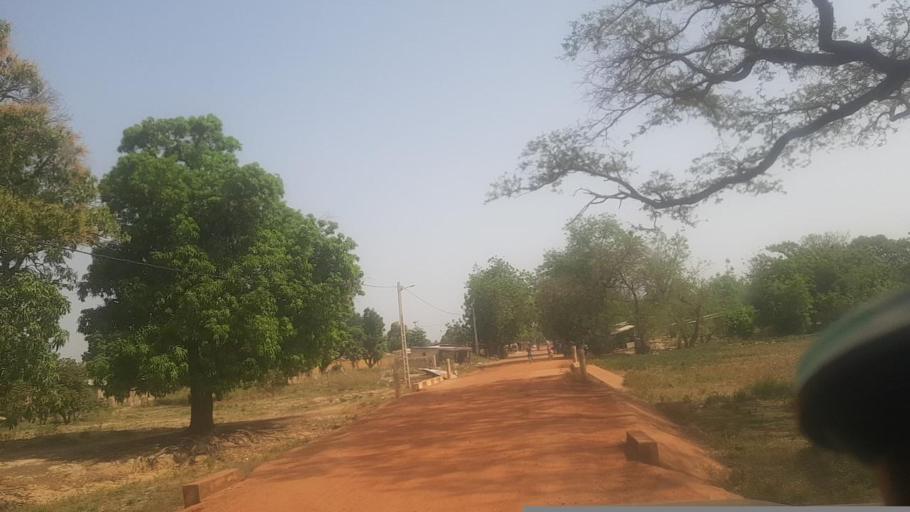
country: ML
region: Segou
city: Bla
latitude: 12.9118
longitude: -6.2424
